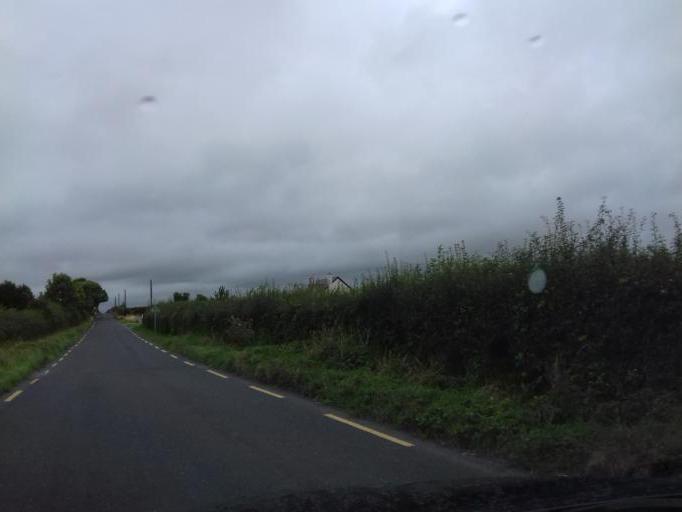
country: IE
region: Leinster
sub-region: Kilkenny
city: Graiguenamanagh
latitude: 52.6109
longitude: -7.0299
